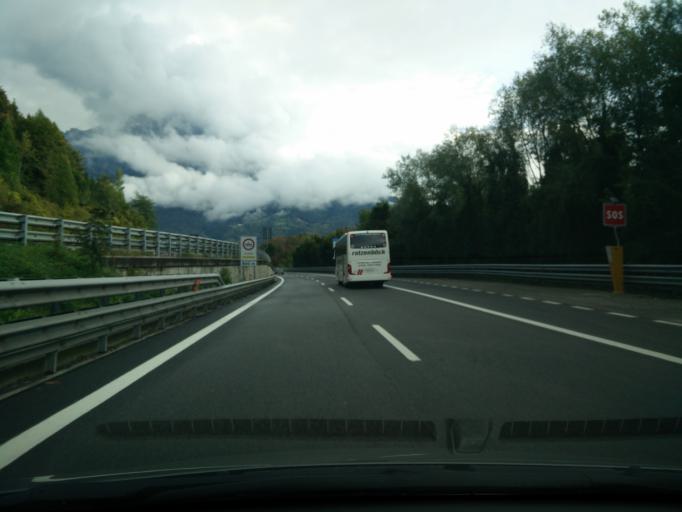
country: IT
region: Veneto
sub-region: Provincia di Belluno
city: Soccher-Paiane-Casan-Arsie
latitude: 46.1439
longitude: 12.3165
